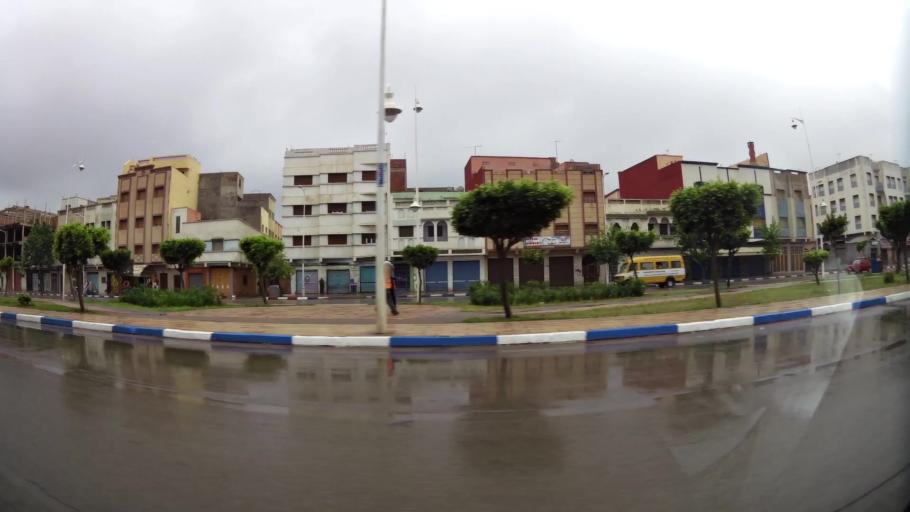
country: MA
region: Oriental
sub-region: Nador
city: Nador
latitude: 35.1671
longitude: -2.9485
